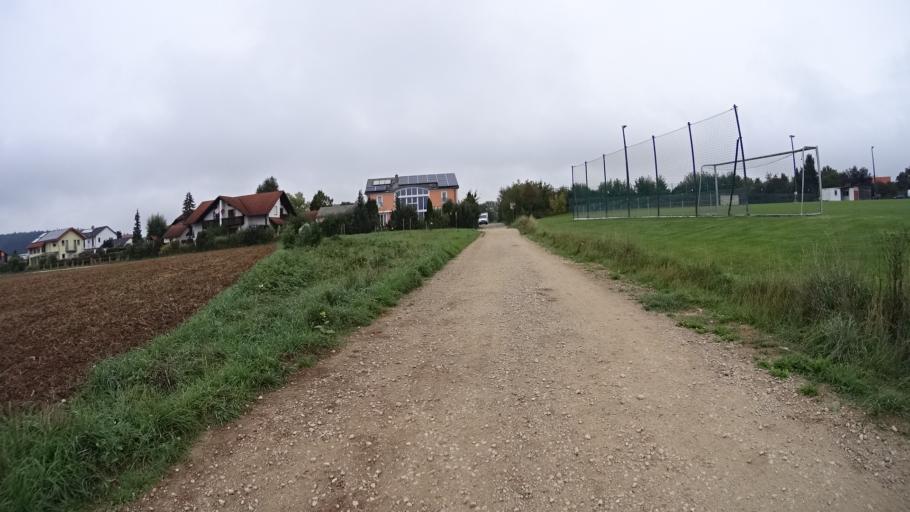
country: DE
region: Bavaria
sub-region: Upper Bavaria
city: Denkendorf
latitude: 48.9214
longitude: 11.4501
